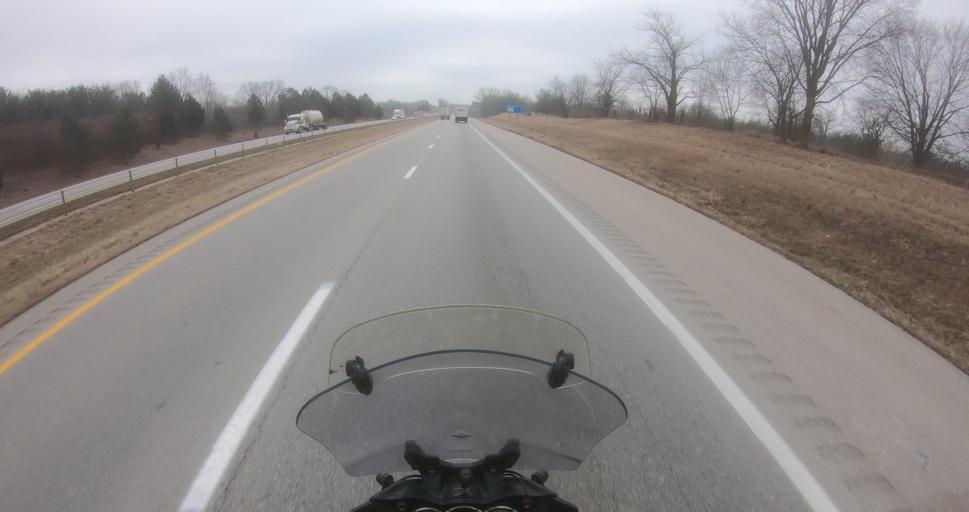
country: US
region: Ohio
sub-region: Miami County
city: Piqua
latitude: 40.1856
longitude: -84.2132
